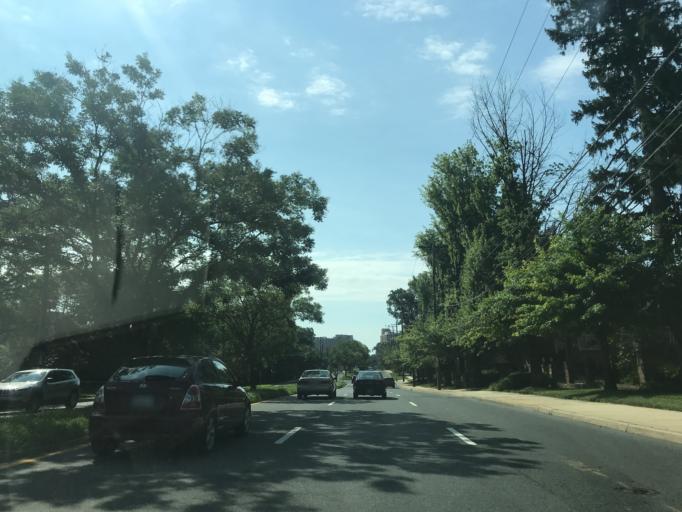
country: US
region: Maryland
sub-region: Montgomery County
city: Silver Spring
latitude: 39.0041
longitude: -77.0370
